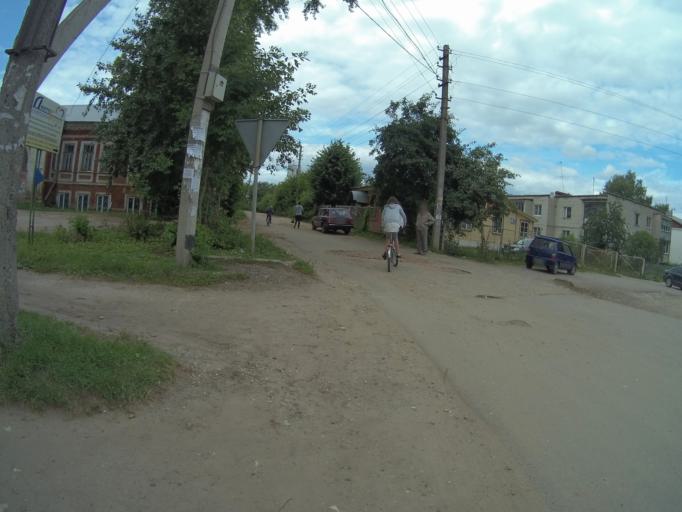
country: RU
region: Vladimir
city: Bogolyubovo
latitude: 56.1981
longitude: 40.5400
